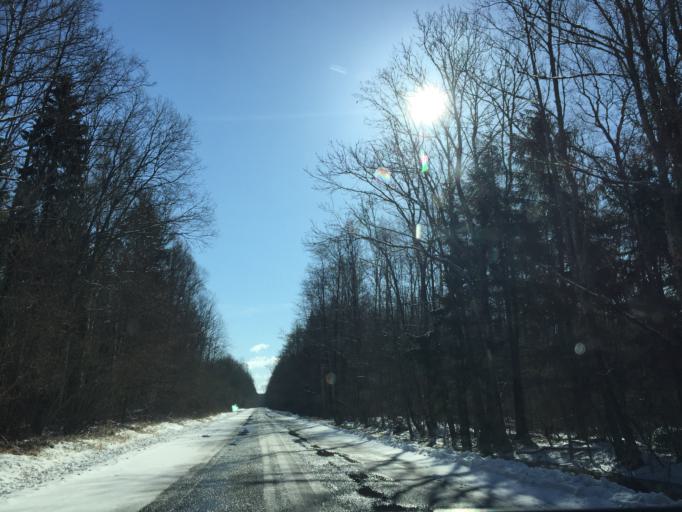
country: LV
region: Salacgrivas
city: Ainazi
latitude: 58.0016
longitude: 24.5201
